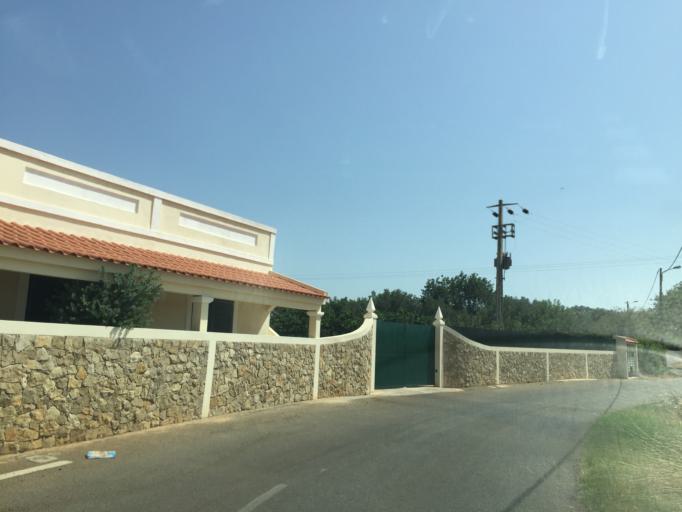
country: PT
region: Faro
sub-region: Albufeira
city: Ferreiras
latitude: 37.1230
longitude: -8.1972
